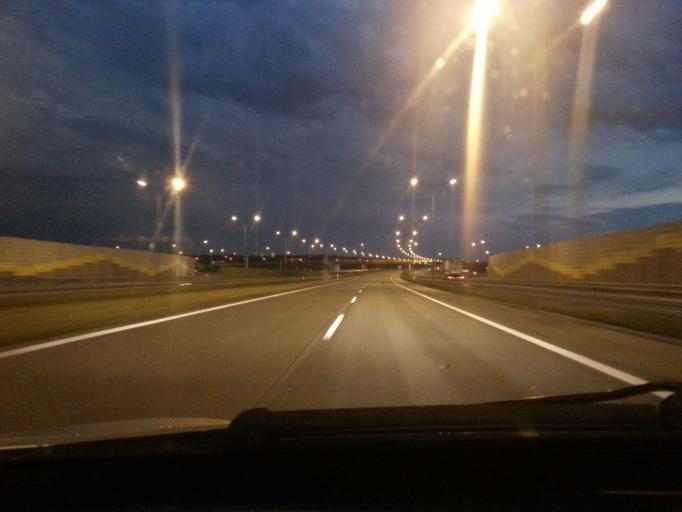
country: PL
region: Lodz Voivodeship
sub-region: Powiat sieradzki
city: Zloczew
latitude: 51.3996
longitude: 18.6176
